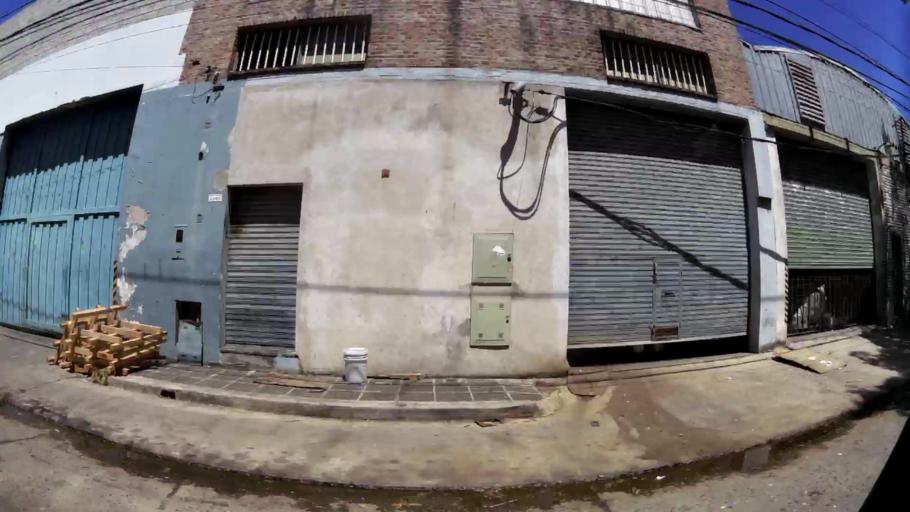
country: AR
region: Buenos Aires
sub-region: Partido de Vicente Lopez
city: Olivos
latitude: -34.5142
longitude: -58.5116
